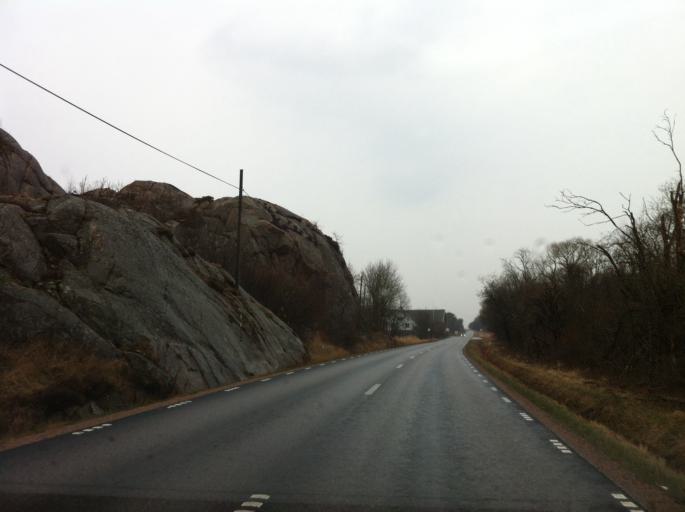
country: SE
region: Vaestra Goetaland
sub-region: Sotenas Kommun
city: Kungshamn
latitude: 58.3811
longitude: 11.2642
